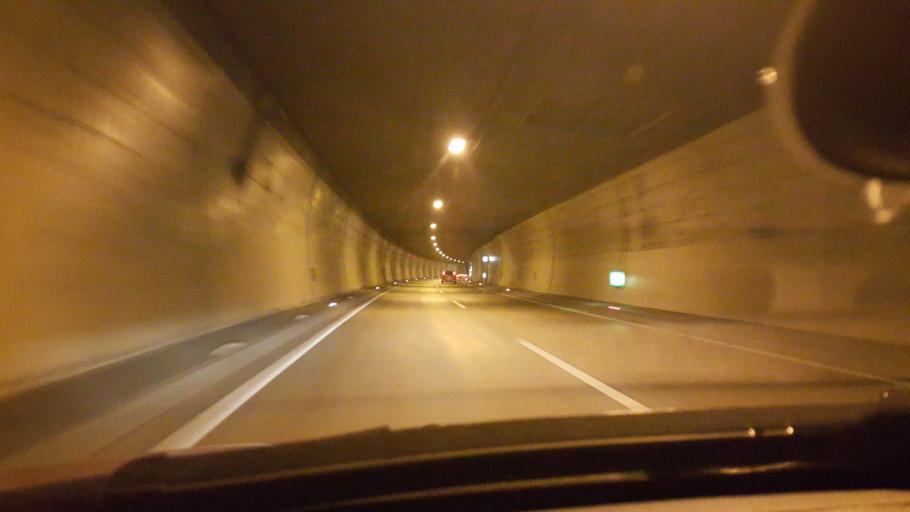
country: AT
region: Styria
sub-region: Graz Stadt
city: Wetzelsdorf
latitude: 47.0416
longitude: 15.4025
